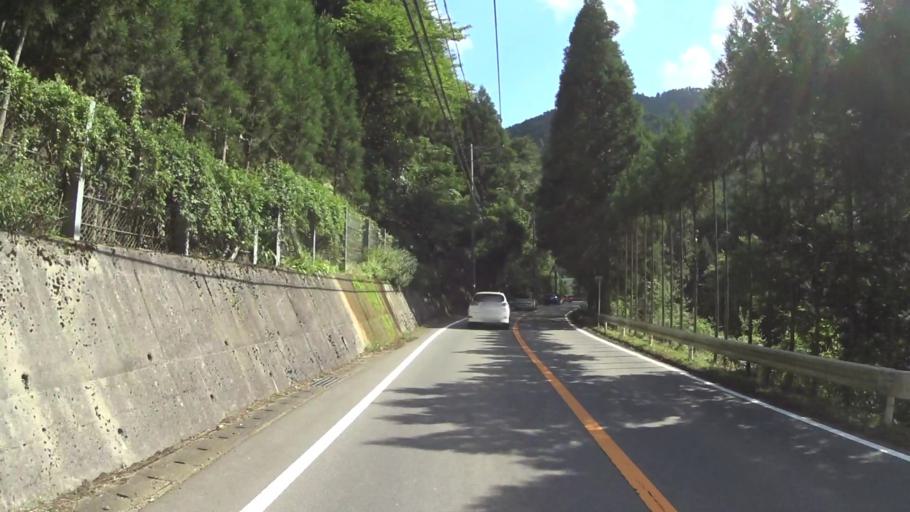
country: JP
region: Kyoto
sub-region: Kyoto-shi
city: Kamigyo-ku
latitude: 35.1018
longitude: 135.6762
